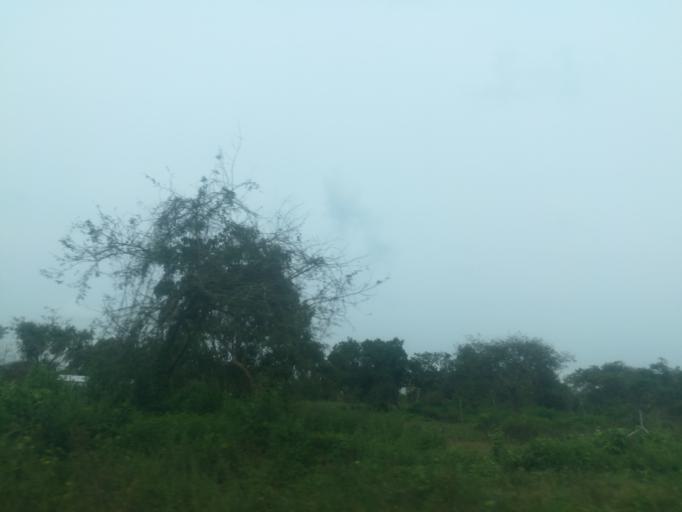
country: NG
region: Ogun
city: Ayetoro
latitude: 7.2744
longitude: 3.0991
